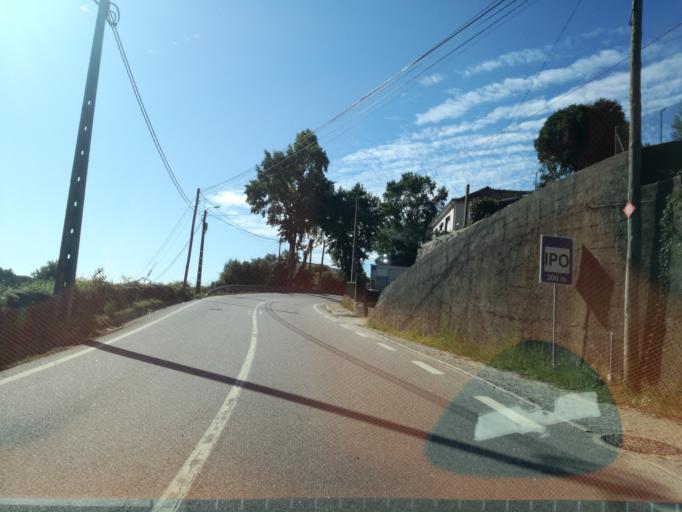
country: PT
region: Porto
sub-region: Pacos de Ferreira
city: Seroa
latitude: 41.2570
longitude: -8.4663
